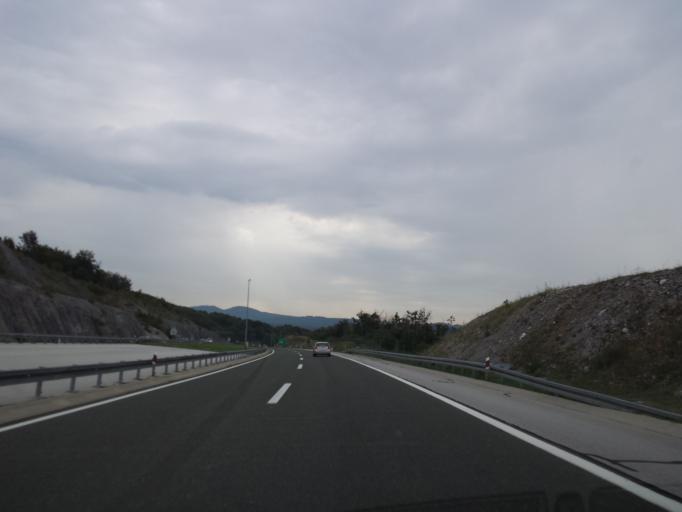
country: HR
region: Licko-Senjska
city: Brinje
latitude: 45.0712
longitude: 15.2057
